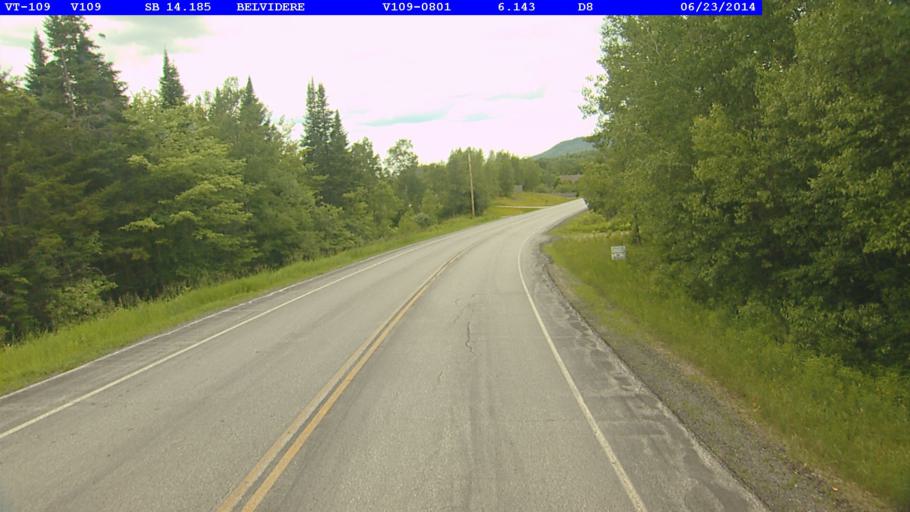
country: US
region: Vermont
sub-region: Lamoille County
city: Johnson
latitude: 44.7623
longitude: -72.6344
